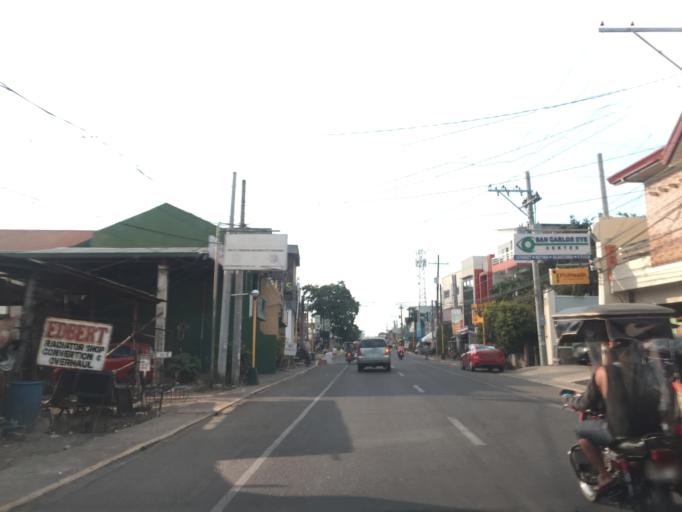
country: PH
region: Ilocos
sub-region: Province of Pangasinan
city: Bolingit
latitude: 15.9318
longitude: 120.3479
